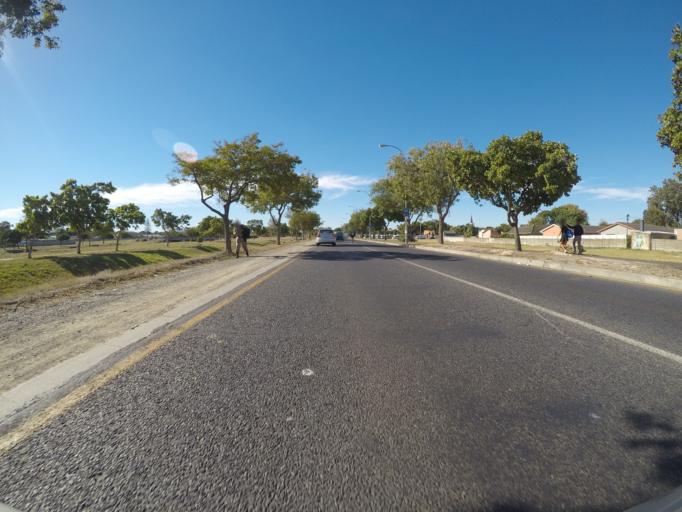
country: ZA
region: Western Cape
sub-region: City of Cape Town
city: Kraaifontein
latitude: -33.9284
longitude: 18.6767
